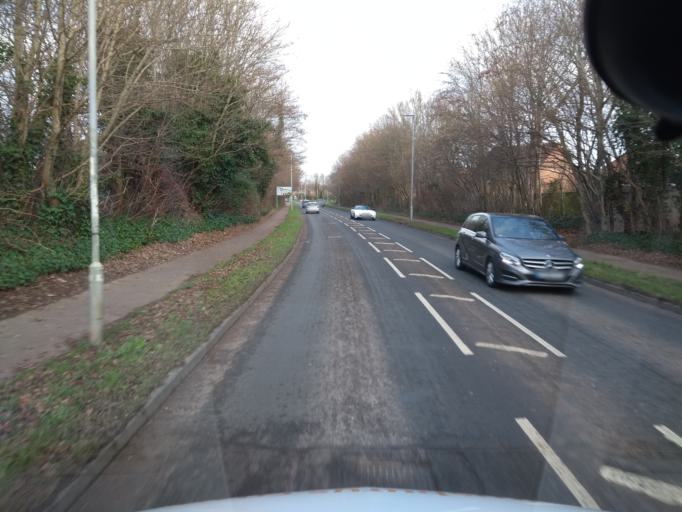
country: GB
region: England
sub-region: Somerset
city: Taunton
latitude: 51.0079
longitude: -3.0757
